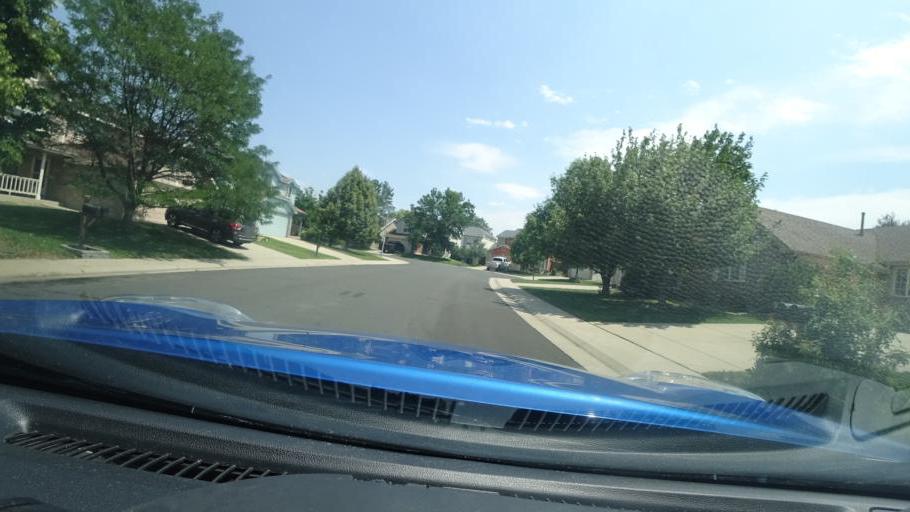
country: US
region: Colorado
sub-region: Adams County
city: Aurora
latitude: 39.6659
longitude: -104.7692
